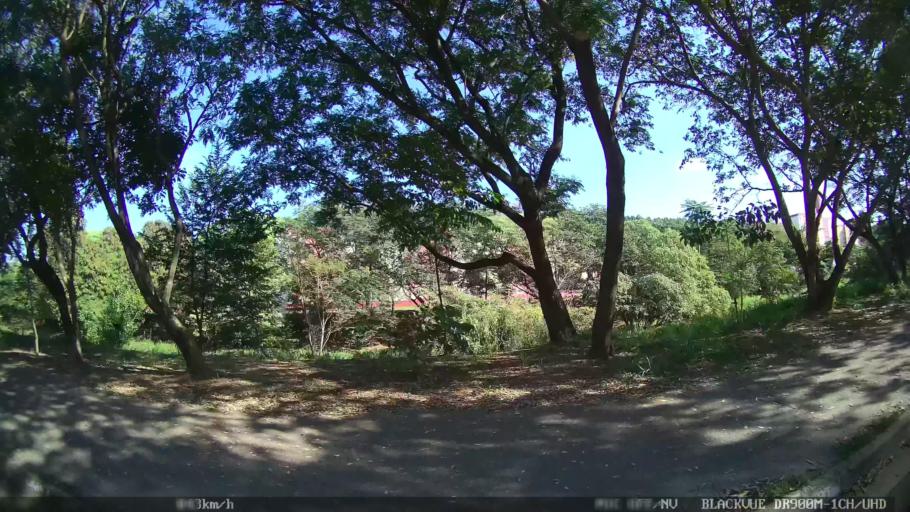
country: BR
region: Sao Paulo
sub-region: Campinas
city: Campinas
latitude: -22.9452
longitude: -47.1242
